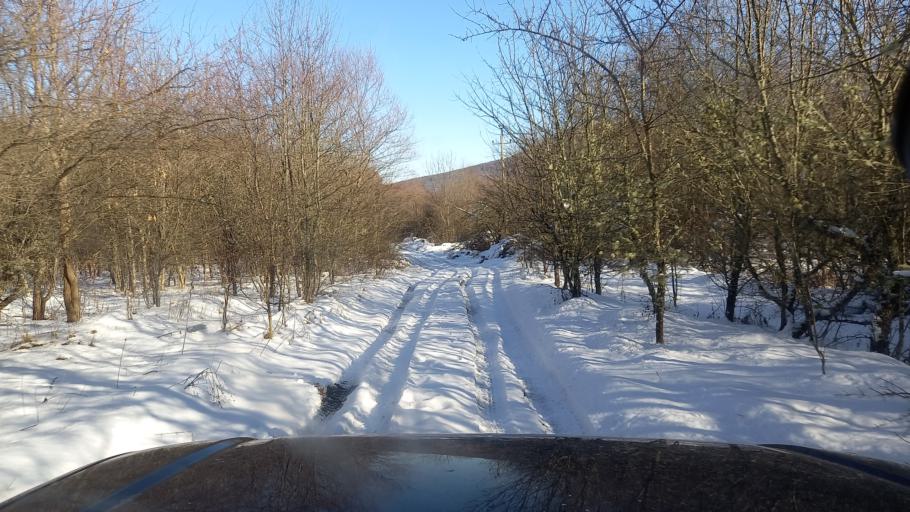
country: RU
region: Adygeya
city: Kamennomostskiy
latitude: 44.2053
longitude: 40.1446
